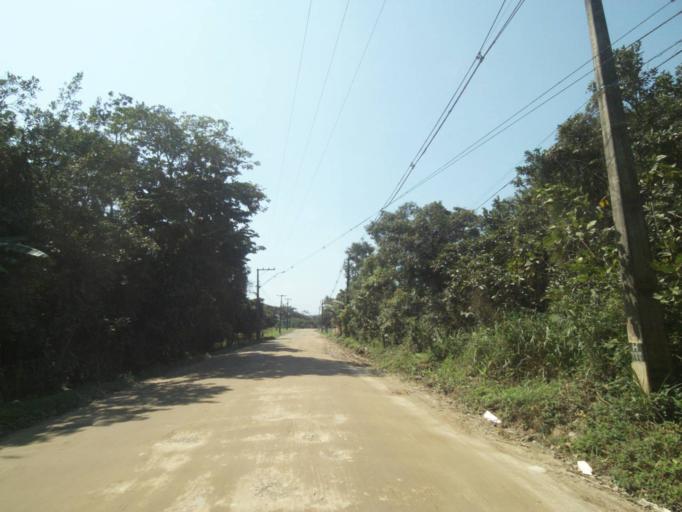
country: BR
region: Parana
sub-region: Paranagua
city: Paranagua
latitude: -25.5610
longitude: -48.6104
